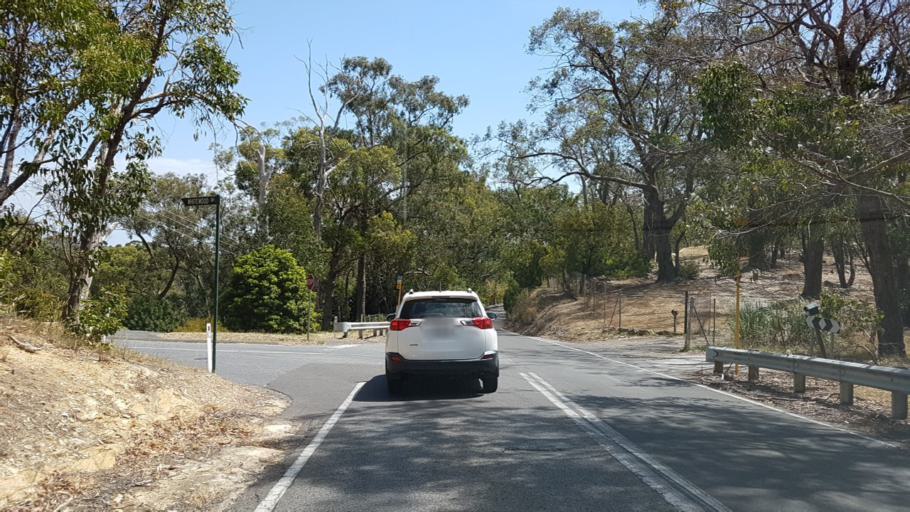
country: AU
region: South Australia
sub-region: Adelaide Hills
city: Upper Sturt
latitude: -35.0163
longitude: 138.6925
